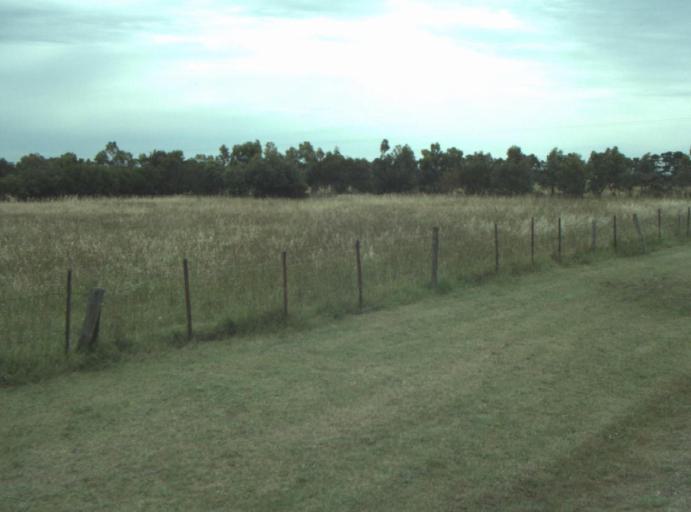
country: AU
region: Victoria
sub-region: Greater Geelong
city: Leopold
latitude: -38.2113
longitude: 144.4505
